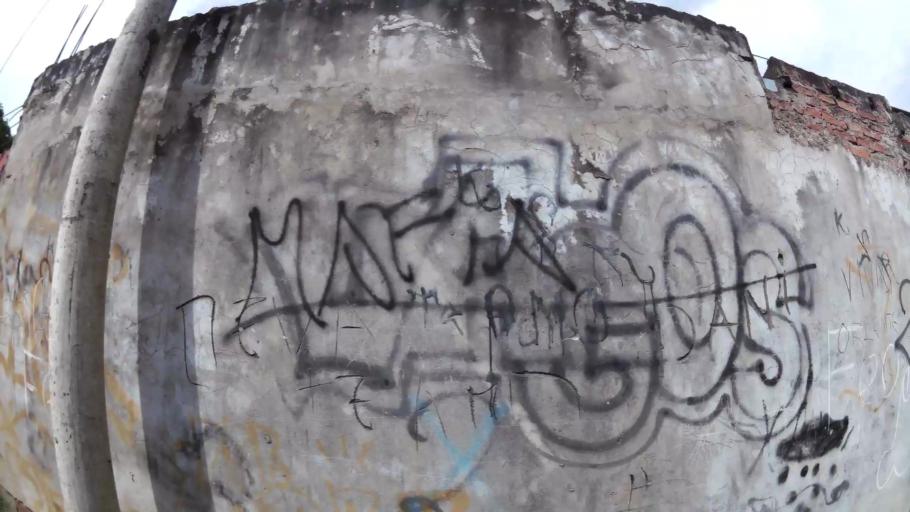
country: BO
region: Santa Cruz
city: Santa Cruz de la Sierra
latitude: -17.7787
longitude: -63.2075
